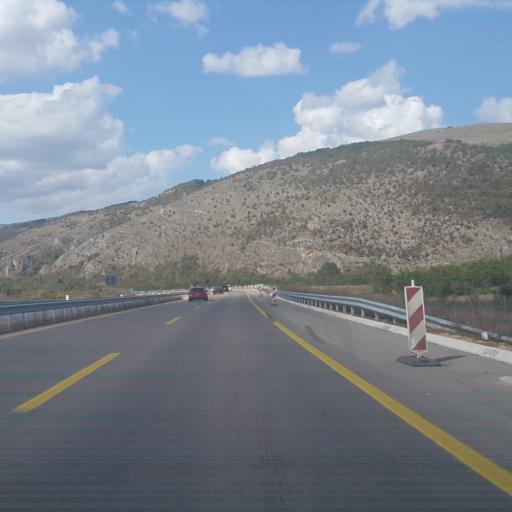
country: RS
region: Central Serbia
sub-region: Pirotski Okrug
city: Bela Palanka
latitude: 43.2297
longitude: 22.3809
